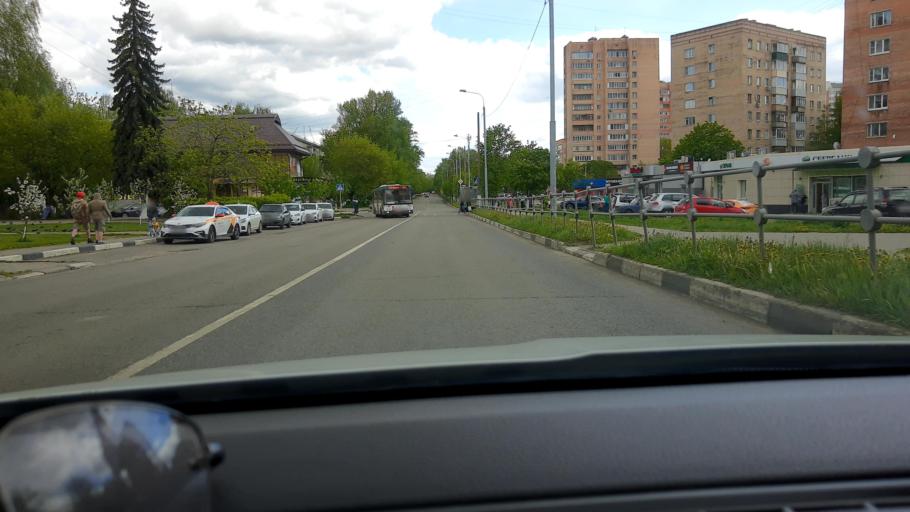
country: RU
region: Moskovskaya
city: Zheleznodorozhnyy
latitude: 55.7428
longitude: 38.0162
